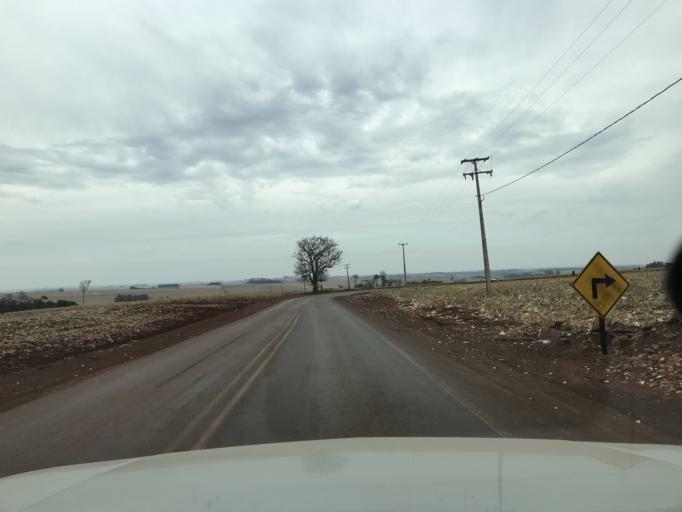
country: BR
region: Parana
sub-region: Palotina
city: Palotina
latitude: -24.4198
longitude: -53.8828
